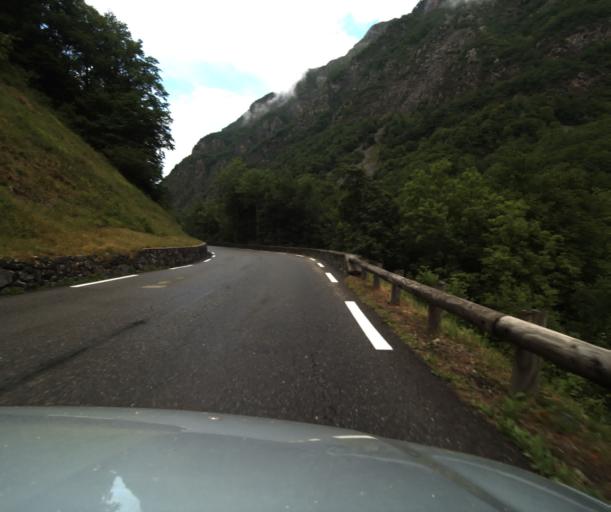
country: FR
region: Midi-Pyrenees
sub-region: Departement des Hautes-Pyrenees
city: Luz-Saint-Sauveur
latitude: 42.8284
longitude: 0.0068
